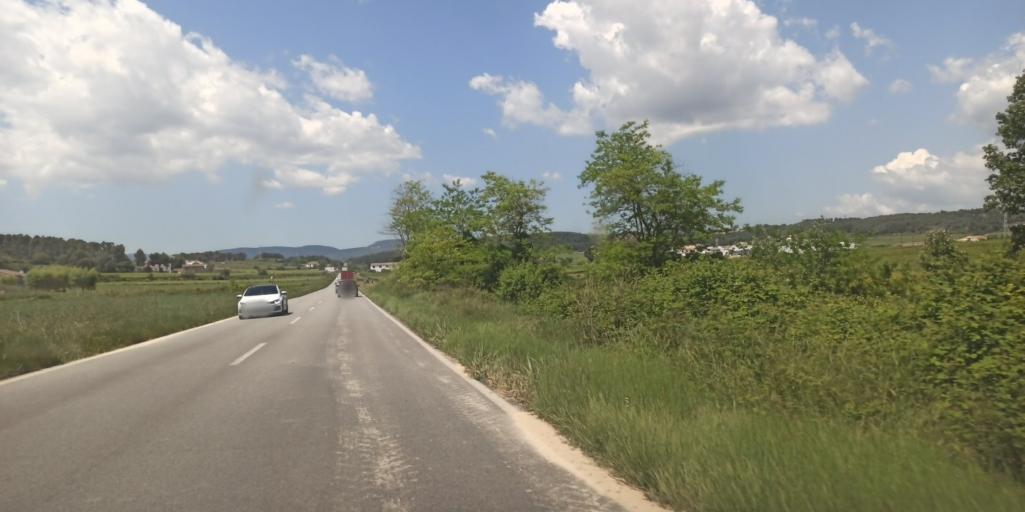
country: ES
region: Catalonia
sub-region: Provincia de Barcelona
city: Vilobi del Penedes
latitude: 41.3645
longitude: 1.6574
